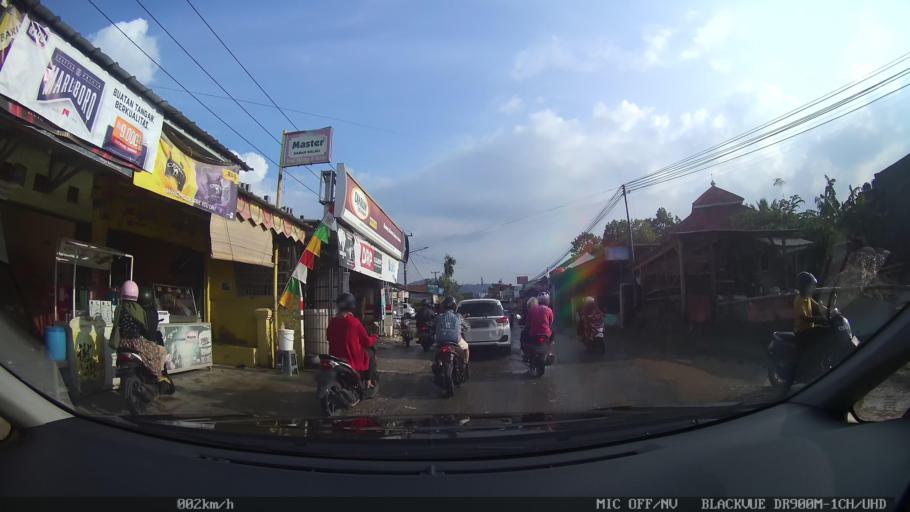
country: ID
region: Lampung
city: Kedaton
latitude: -5.3857
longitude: 105.3158
